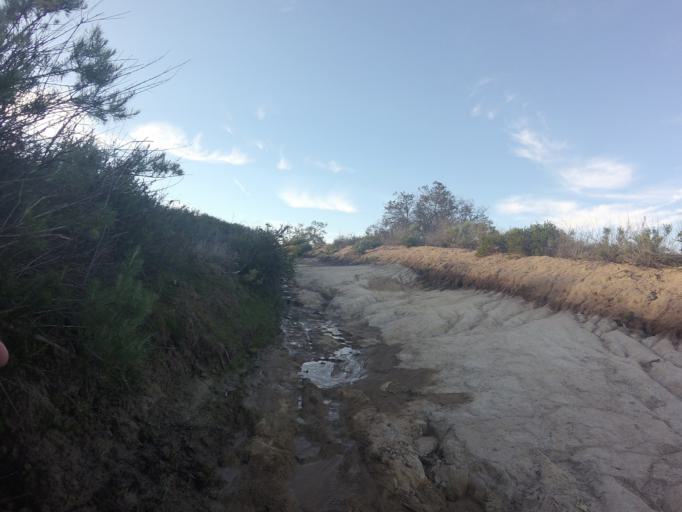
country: US
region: California
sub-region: Orange County
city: Laguna Beach
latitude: 33.5914
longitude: -117.7777
